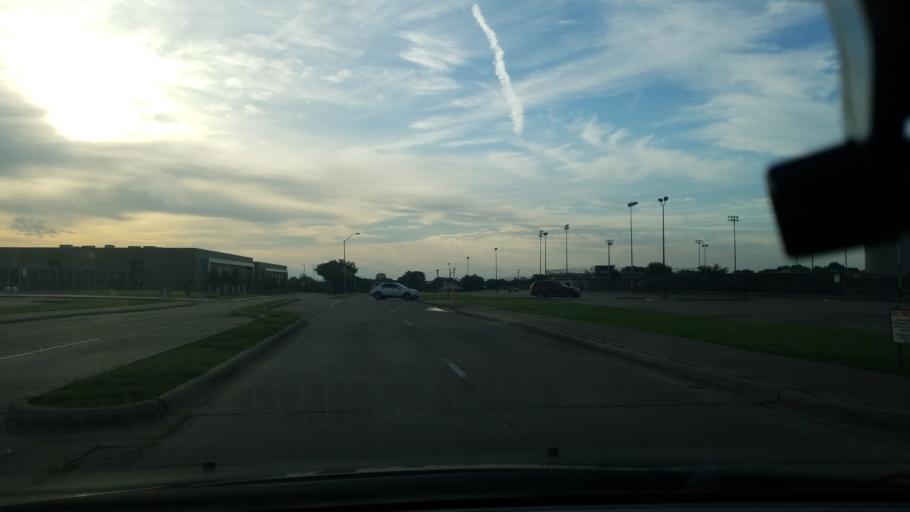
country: US
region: Texas
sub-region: Dallas County
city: Balch Springs
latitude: 32.7623
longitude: -96.6348
